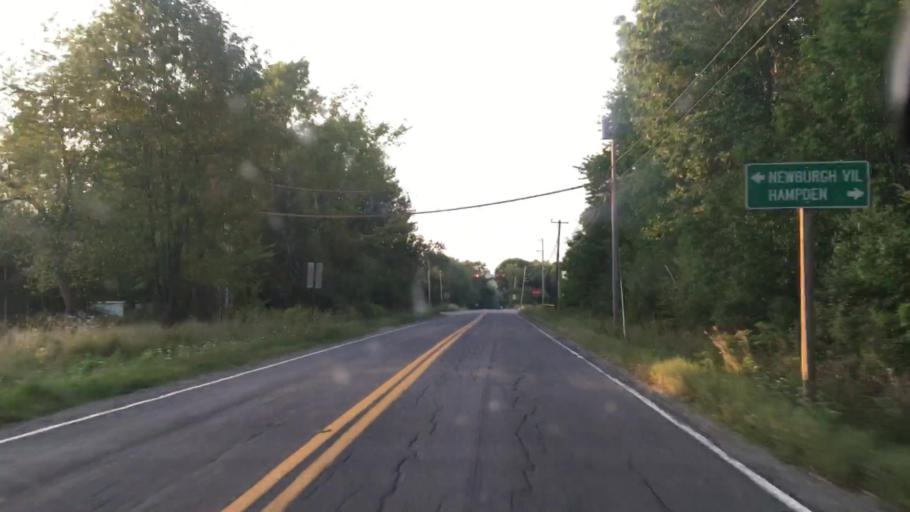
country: US
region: Maine
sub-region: Waldo County
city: Frankfort
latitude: 44.6974
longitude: -68.9438
